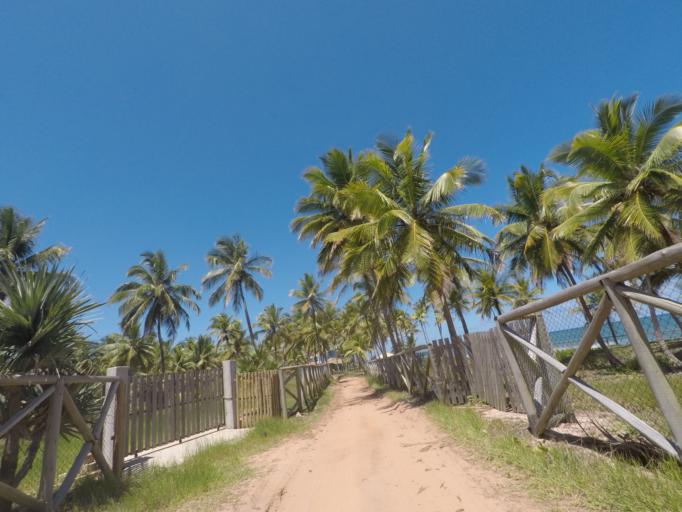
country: BR
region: Bahia
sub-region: Marau
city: Marau
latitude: -14.0184
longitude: -38.9456
